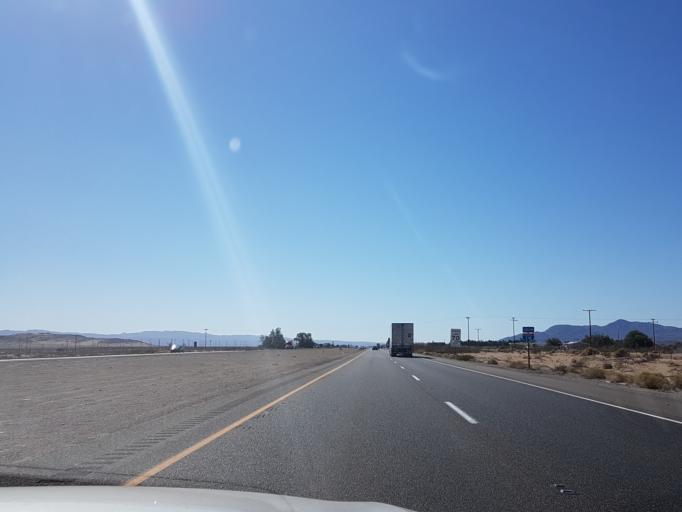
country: US
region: California
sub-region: San Bernardino County
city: Fort Irwin
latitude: 34.9614
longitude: -116.6504
